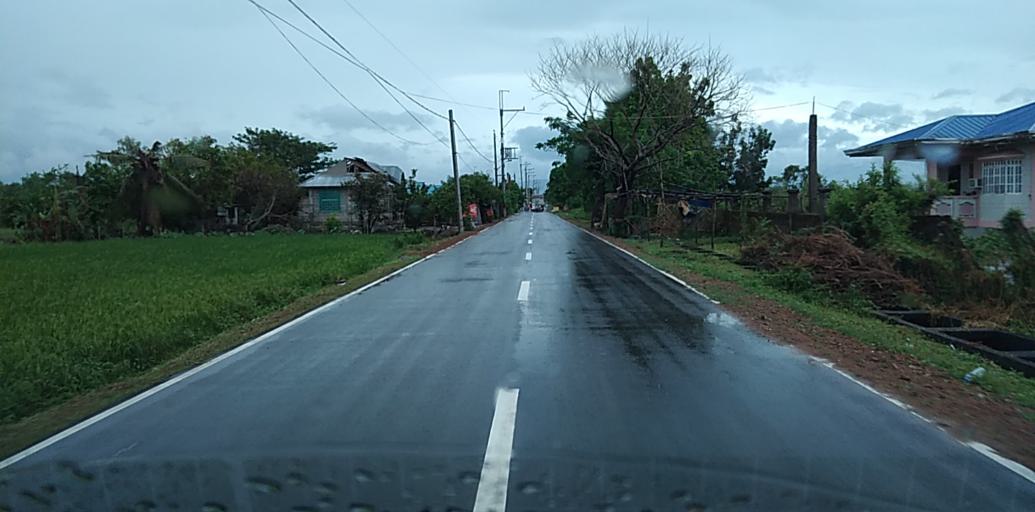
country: PH
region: Central Luzon
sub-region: Province of Pampanga
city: Salapungan
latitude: 15.1351
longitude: 120.9186
